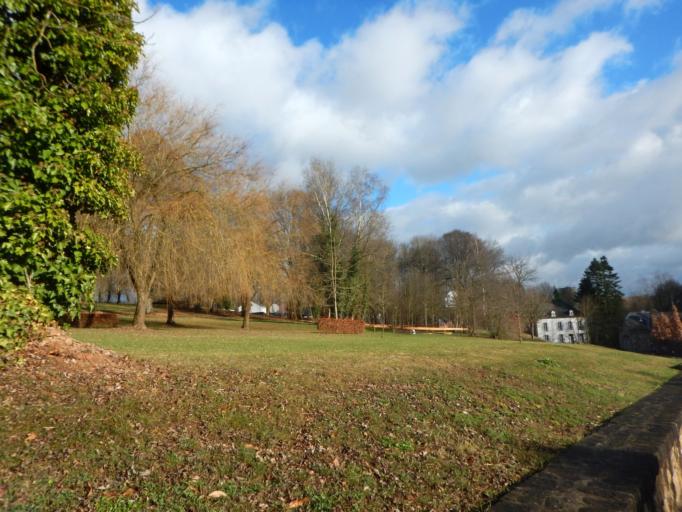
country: LU
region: Diekirch
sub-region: Canton de Redange
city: Redange-sur-Attert
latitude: 49.7641
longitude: 5.8908
